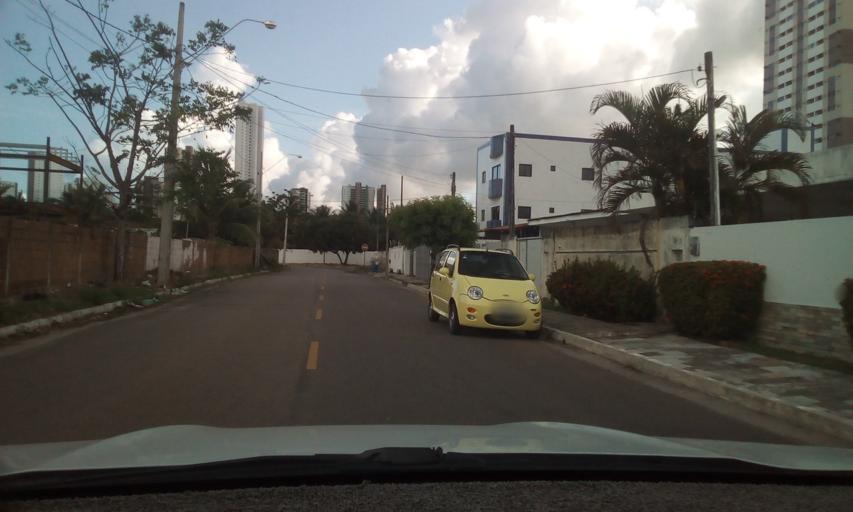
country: BR
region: Paraiba
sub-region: Joao Pessoa
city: Joao Pessoa
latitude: -7.0760
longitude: -34.8426
